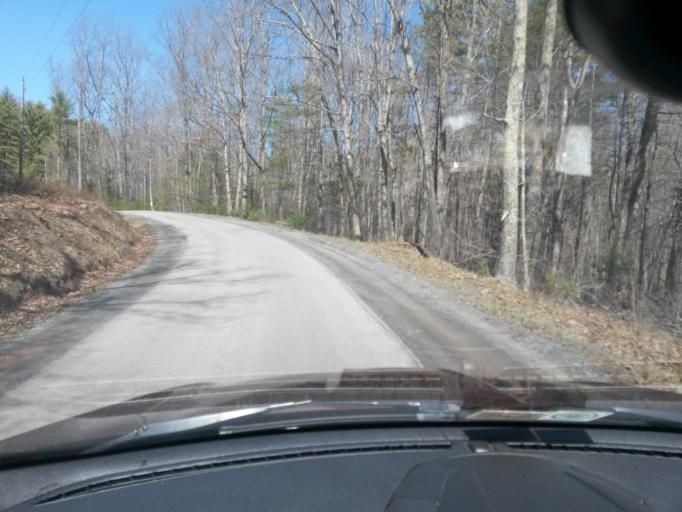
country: US
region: West Virginia
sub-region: Greenbrier County
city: White Sulphur Springs
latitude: 37.6361
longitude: -80.3382
